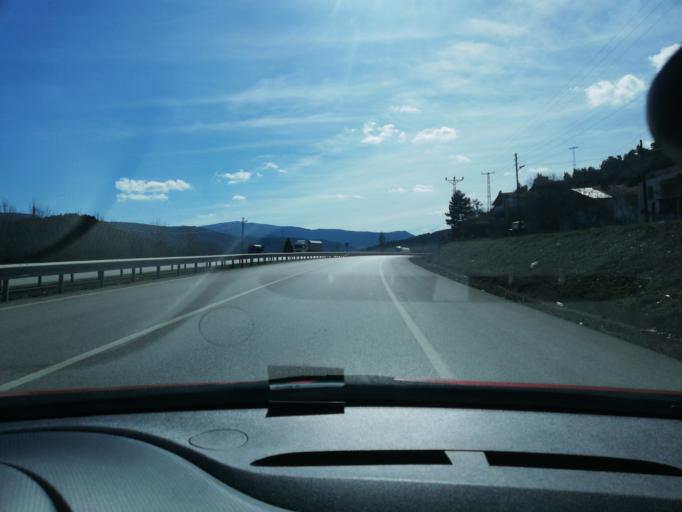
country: TR
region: Karabuk
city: Eskipazar
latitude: 41.0283
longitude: 32.6335
